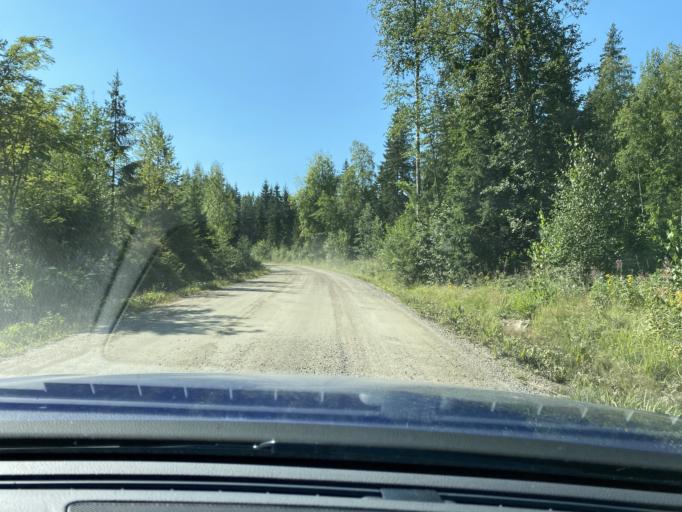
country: FI
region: Central Finland
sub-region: Jyvaeskylae
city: Korpilahti
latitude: 61.8792
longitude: 25.4116
